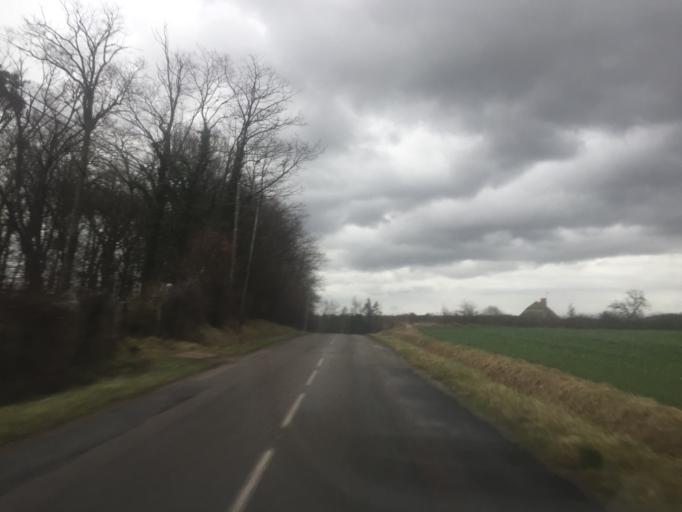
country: FR
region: Franche-Comte
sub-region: Departement de la Haute-Saone
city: Pesmes
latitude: 47.2190
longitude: 5.5111
